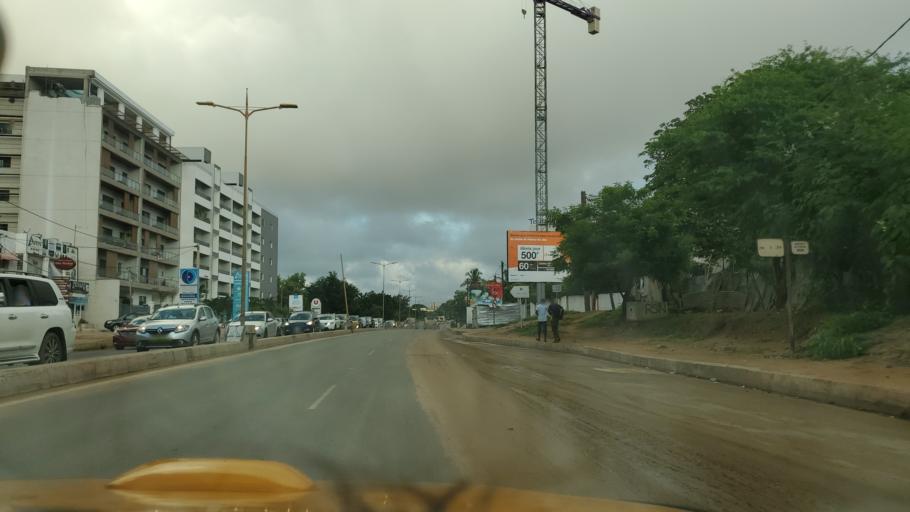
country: SN
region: Dakar
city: Mermoz Boabab
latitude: 14.7176
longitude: -17.4861
